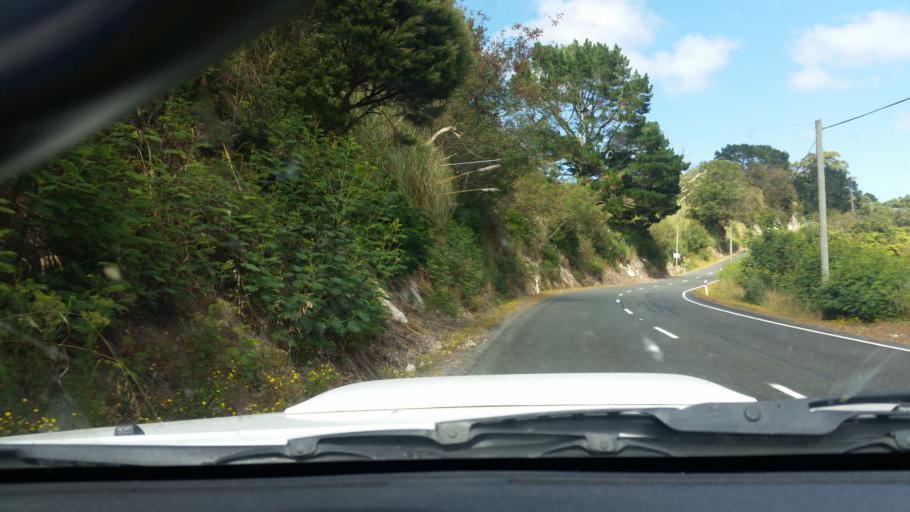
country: NZ
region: Northland
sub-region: Kaipara District
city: Dargaville
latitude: -35.8227
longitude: 173.6960
